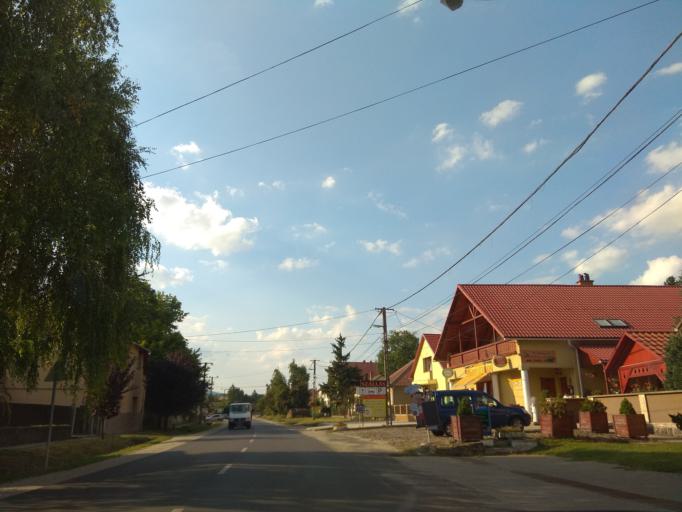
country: HU
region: Borsod-Abauj-Zemplen
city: Harsany
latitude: 47.9656
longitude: 20.7423
